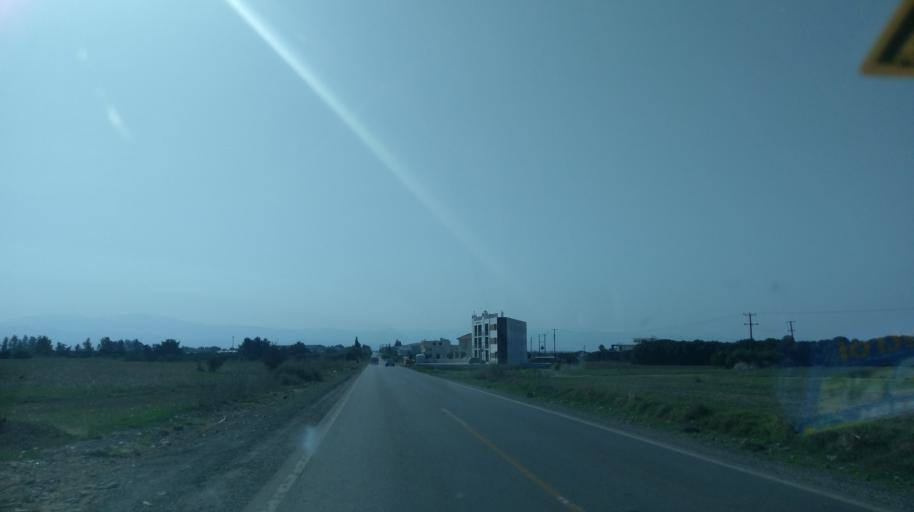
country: CY
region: Lefkosia
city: Morfou
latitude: 35.2395
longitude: 33.0251
